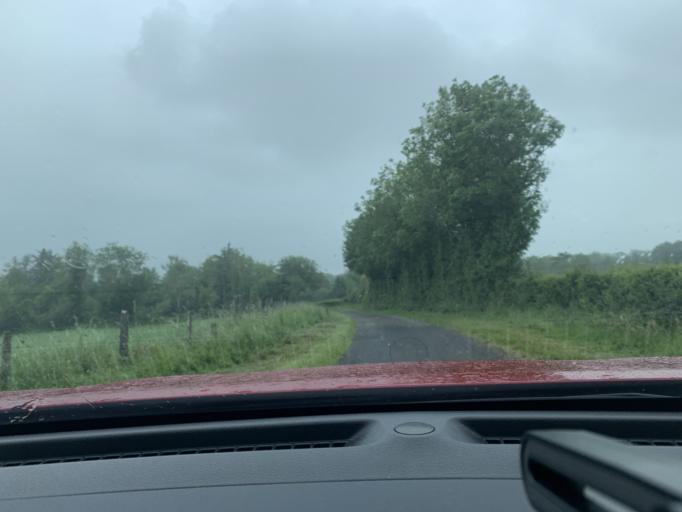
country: GB
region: Northern Ireland
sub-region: Fermanagh District
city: Enniskillen
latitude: 54.2719
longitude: -7.7418
